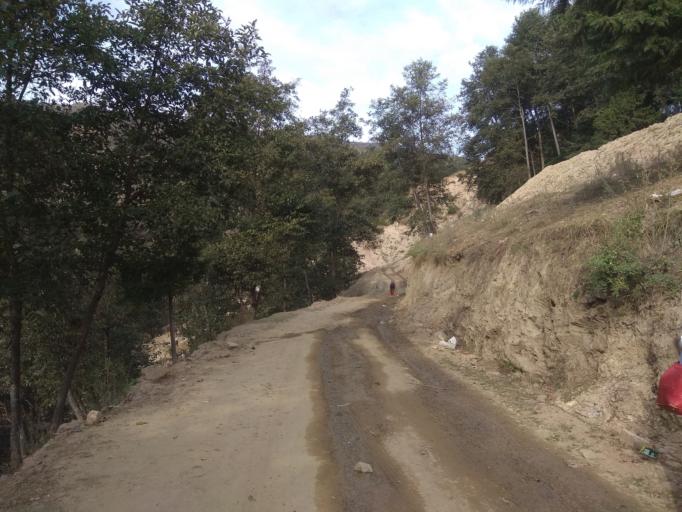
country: NP
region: Far Western
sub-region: Seti Zone
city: Achham
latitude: 29.2517
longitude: 81.6387
